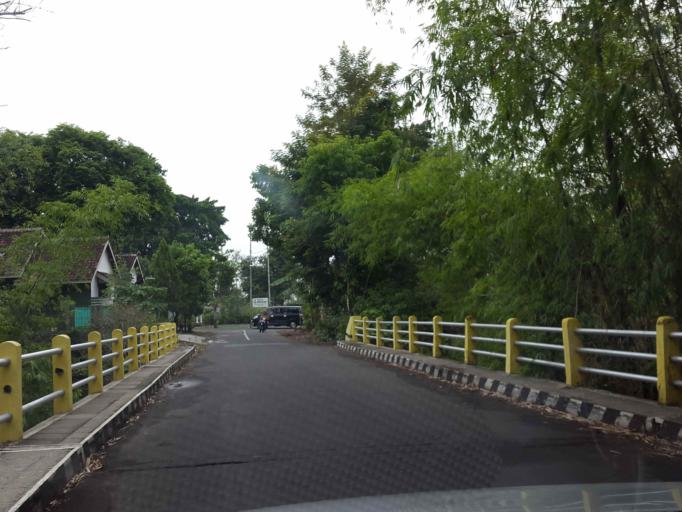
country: ID
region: Central Java
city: Jaten
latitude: -7.6017
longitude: 110.9597
